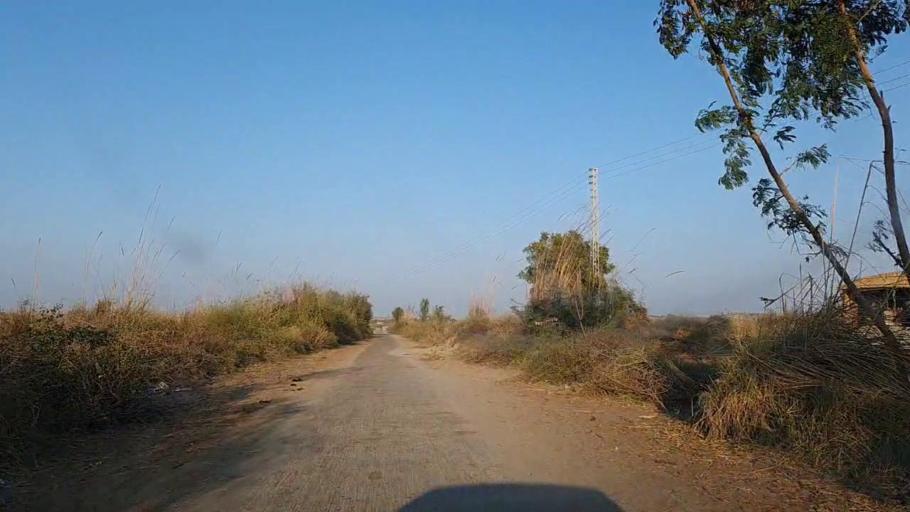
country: PK
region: Sindh
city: Sanghar
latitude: 26.2973
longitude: 68.9879
